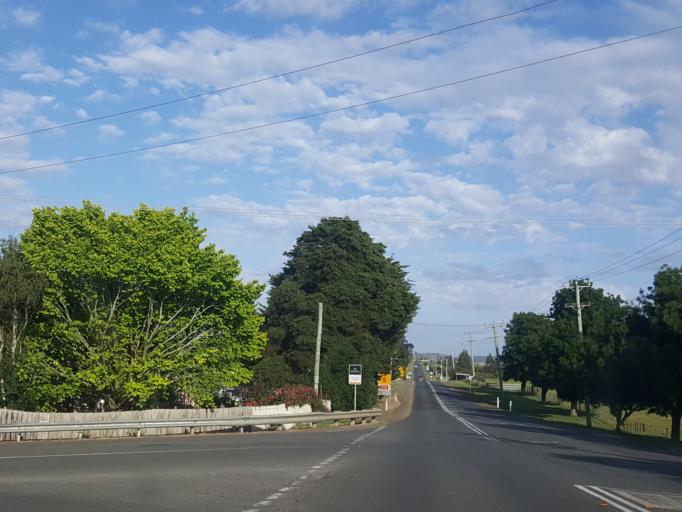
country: AU
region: Tasmania
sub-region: Northern Midlands
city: Evandale
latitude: -41.5671
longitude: 147.2401
